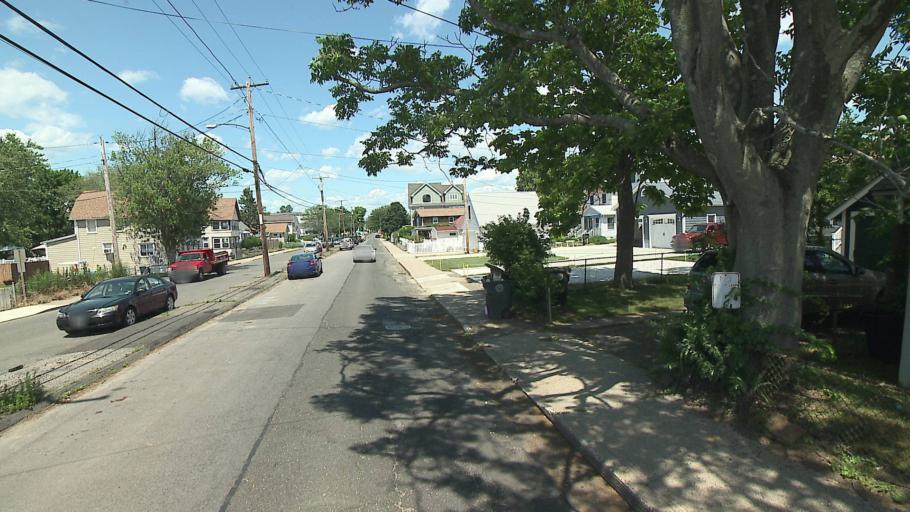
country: US
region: Connecticut
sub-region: New Haven County
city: Milford
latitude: 41.2062
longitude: -73.0614
